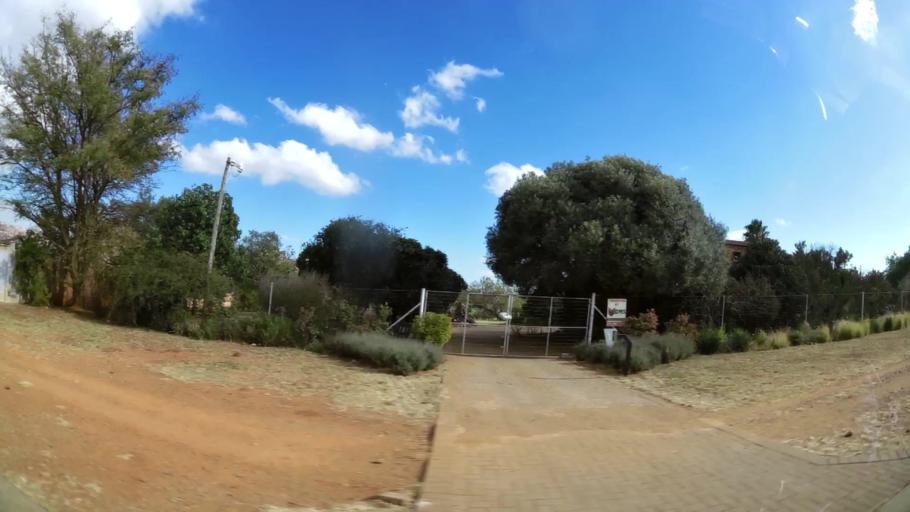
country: ZA
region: Gauteng
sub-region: West Rand District Municipality
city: Muldersdriseloop
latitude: -26.0832
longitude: 27.8549
